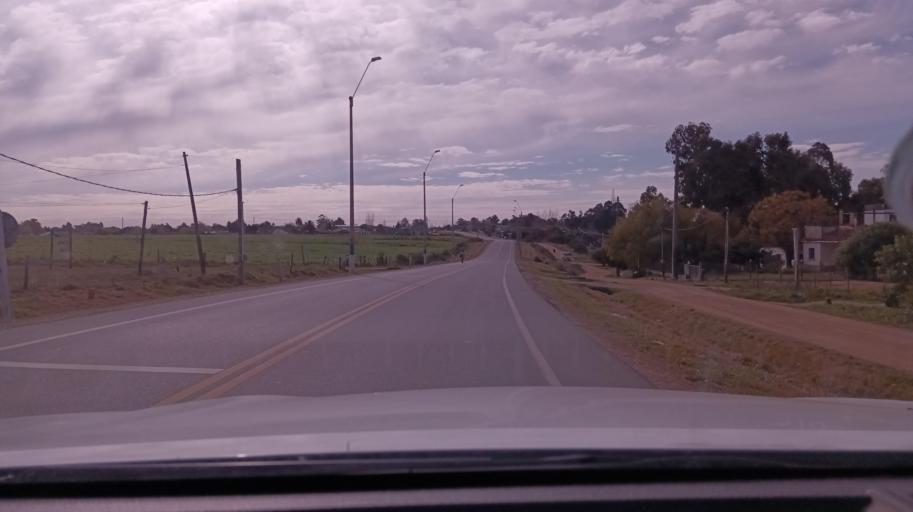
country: UY
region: Canelones
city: Toledo
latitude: -34.7453
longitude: -56.1120
